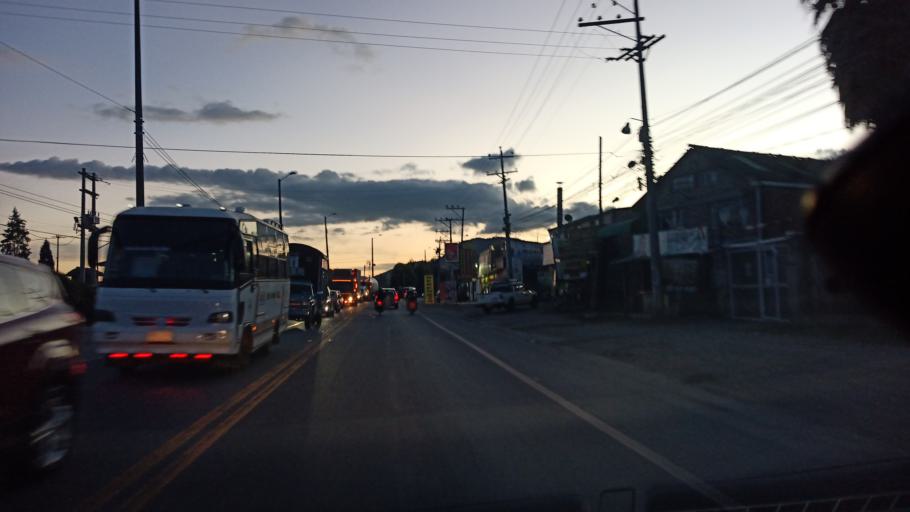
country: CO
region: Cundinamarca
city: Chia
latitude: 4.8509
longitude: -74.0730
